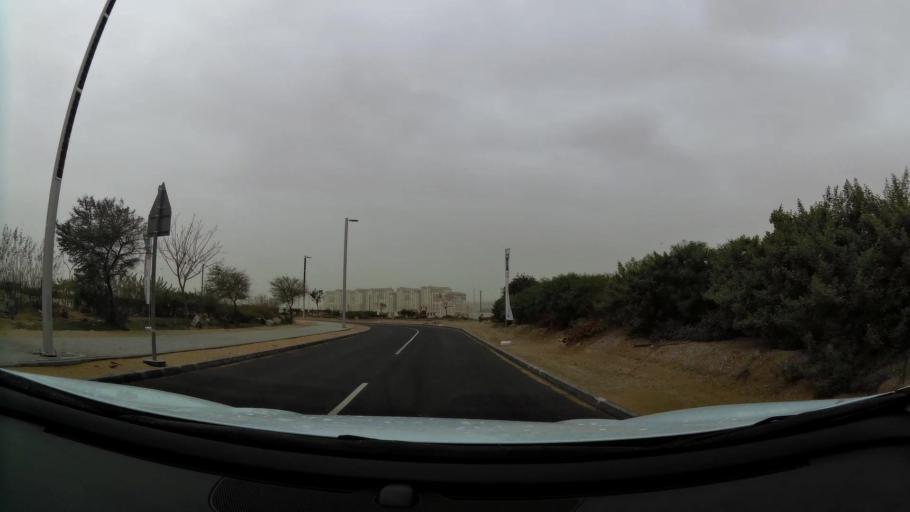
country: AE
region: Abu Dhabi
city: Abu Dhabi
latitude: 24.4385
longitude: 54.6172
